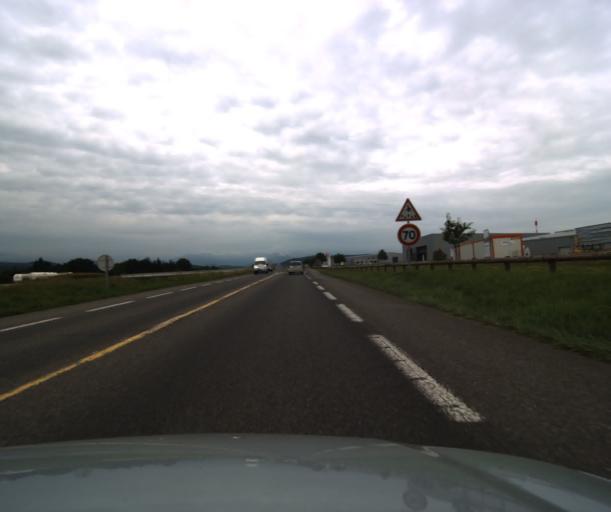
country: FR
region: Midi-Pyrenees
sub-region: Departement des Hautes-Pyrenees
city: Ossun
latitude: 43.1734
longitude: 0.0008
